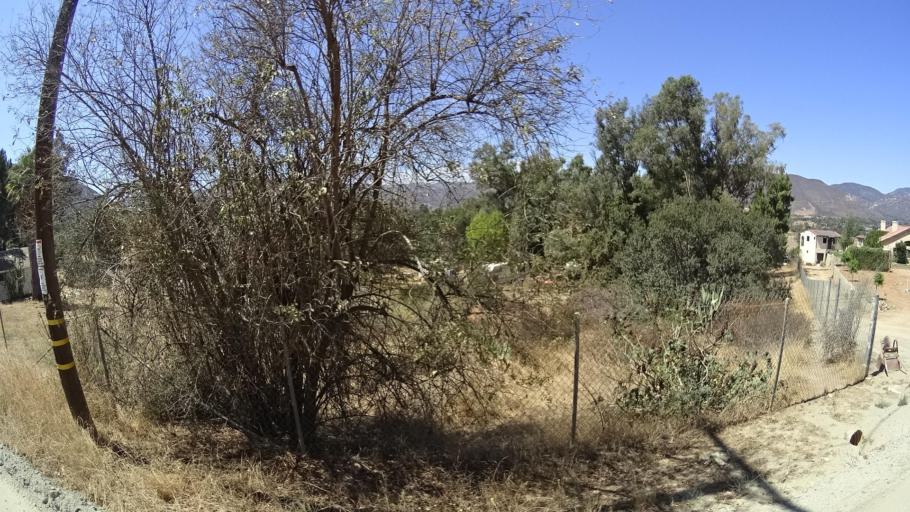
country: US
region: California
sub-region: San Diego County
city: Rainbow
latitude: 33.3550
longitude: -117.0678
